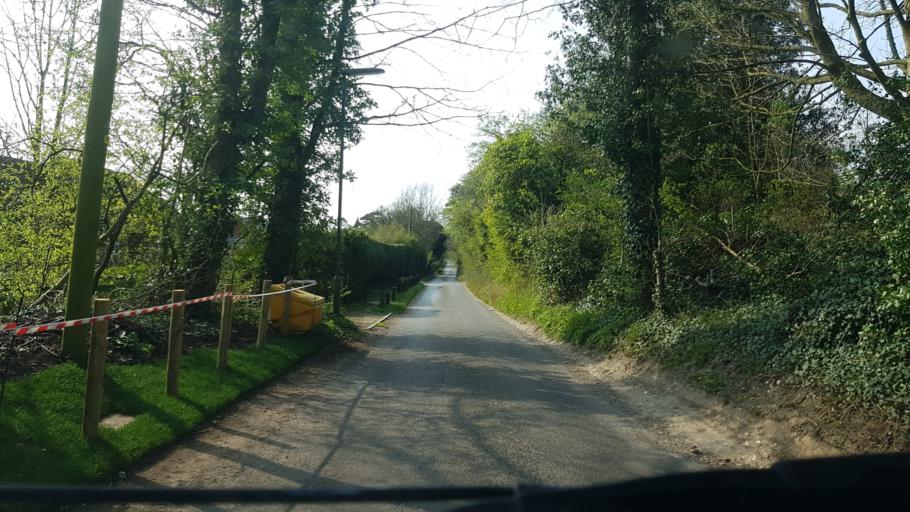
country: GB
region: England
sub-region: Surrey
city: Chilworth
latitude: 51.2315
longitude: -0.5298
